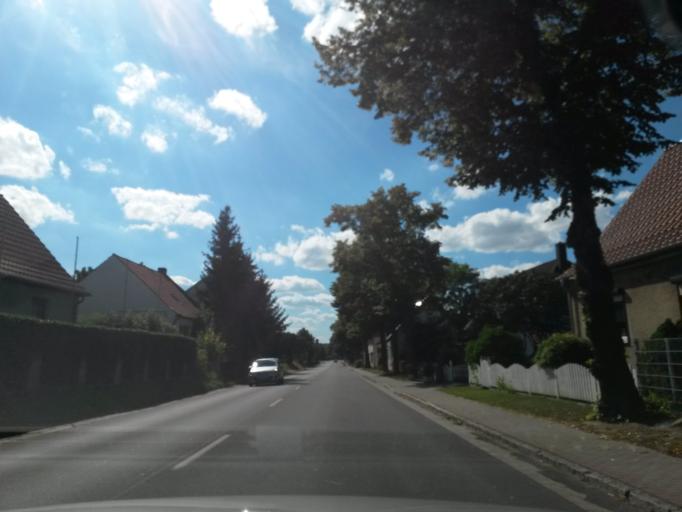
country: DE
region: Brandenburg
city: Schoneberg
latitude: 53.0315
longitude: 14.1756
